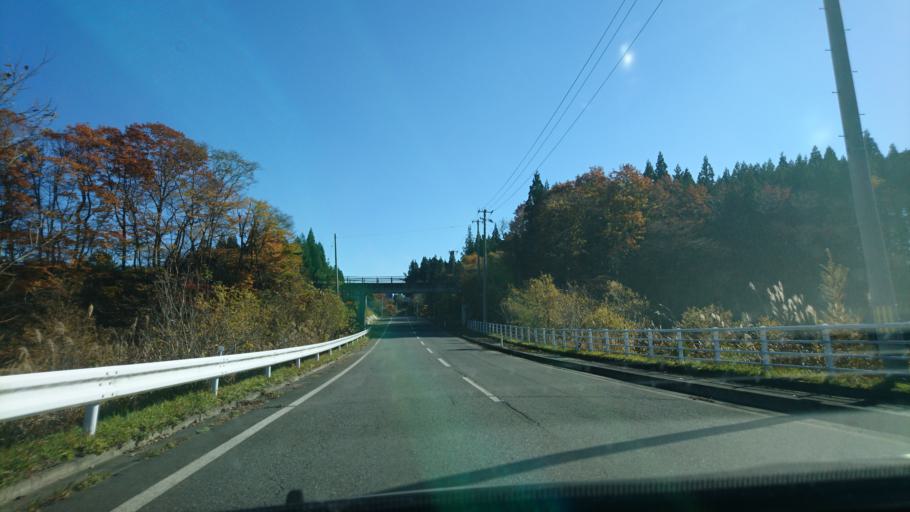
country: JP
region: Iwate
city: Mizusawa
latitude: 39.1197
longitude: 140.9493
